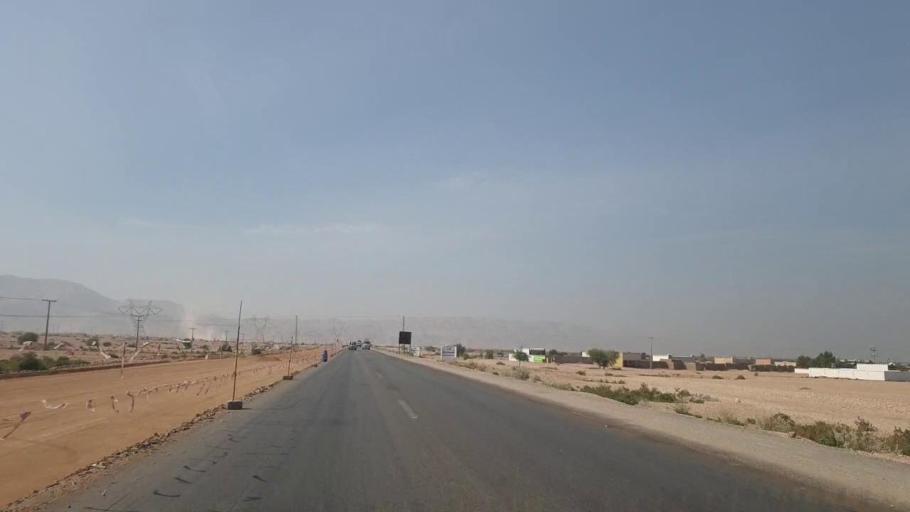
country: PK
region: Sindh
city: Sehwan
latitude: 26.2034
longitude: 67.9343
